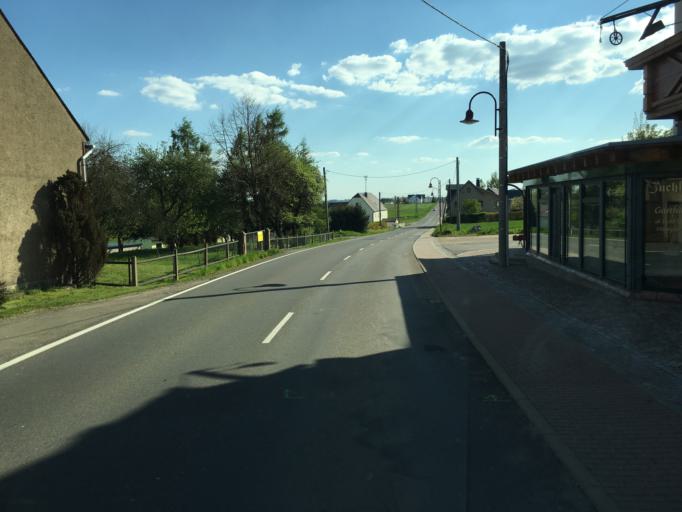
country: DE
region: Saxony
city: Hainichen
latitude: 51.0015
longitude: 13.1271
